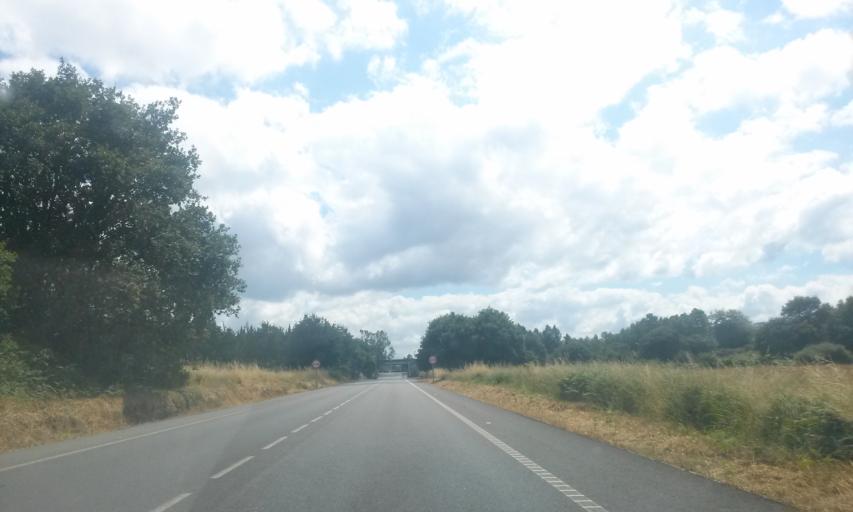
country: ES
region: Galicia
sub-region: Provincia de Lugo
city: Rabade
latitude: 43.1246
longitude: -7.6259
